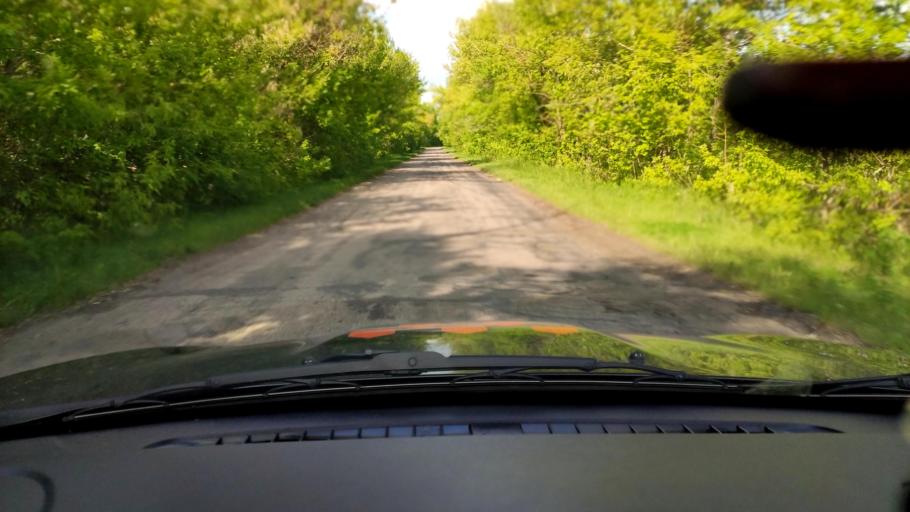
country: RU
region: Voronezj
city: Uryv-Pokrovka
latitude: 51.2033
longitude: 39.0684
